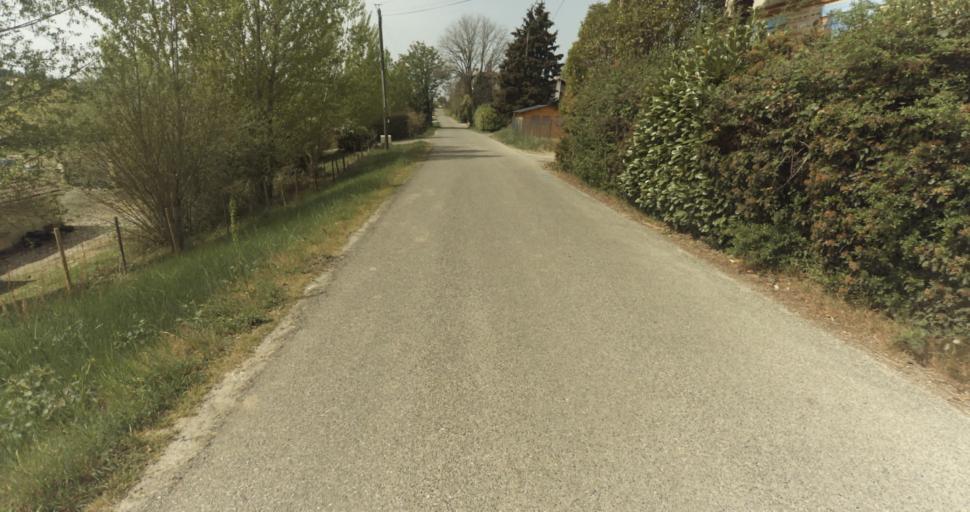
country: FR
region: Midi-Pyrenees
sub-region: Departement du Tarn-et-Garonne
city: Moissac
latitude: 44.1152
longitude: 1.0803
